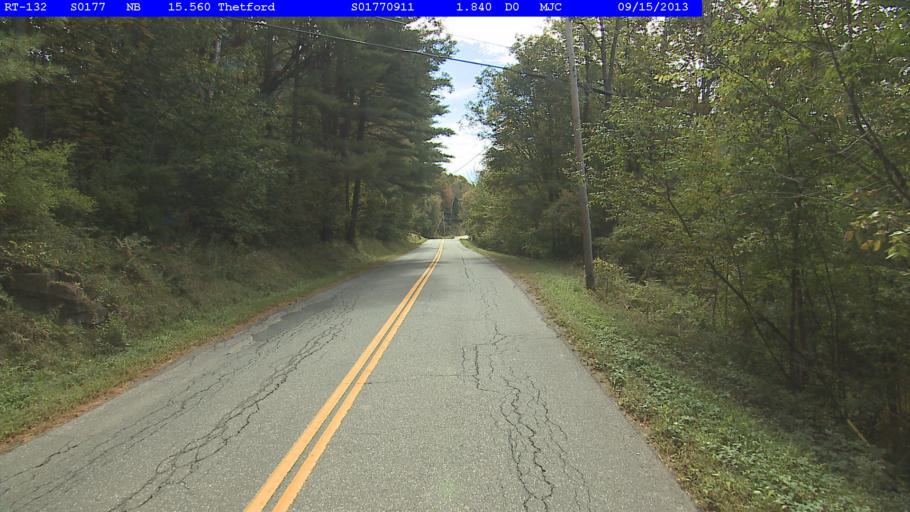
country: US
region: New Hampshire
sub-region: Grafton County
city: Hanover
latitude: 43.8283
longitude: -72.2881
